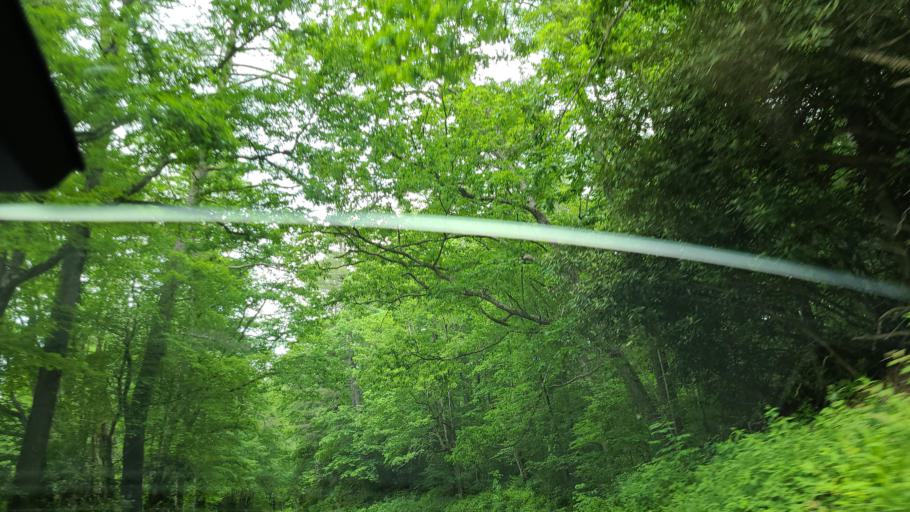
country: US
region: North Carolina
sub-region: Macon County
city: Franklin
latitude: 35.0758
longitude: -83.2449
